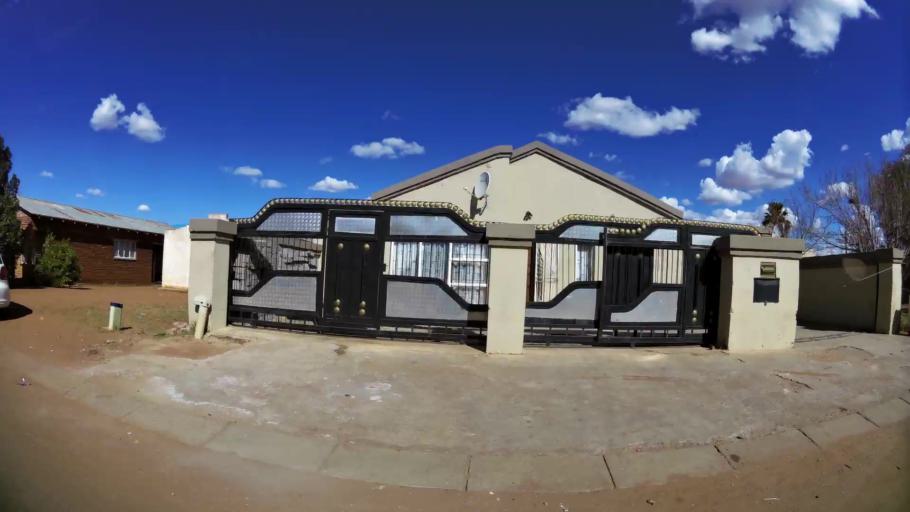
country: ZA
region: North-West
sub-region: Dr Kenneth Kaunda District Municipality
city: Klerksdorp
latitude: -26.8686
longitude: 26.5841
